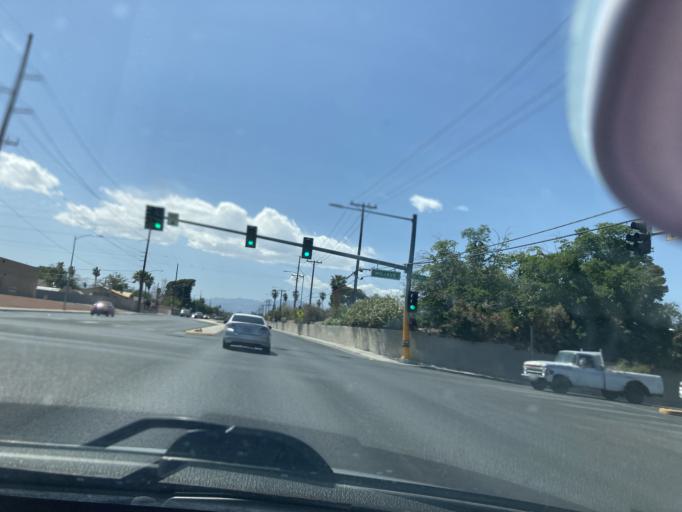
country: US
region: Nevada
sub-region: Clark County
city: North Las Vegas
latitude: 36.1811
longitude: -115.1070
